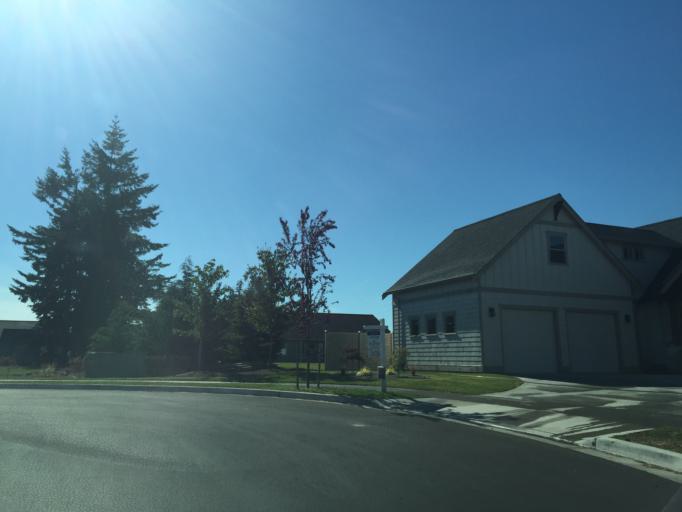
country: US
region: Washington
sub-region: Whatcom County
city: Lynden
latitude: 48.9610
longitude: -122.4172
